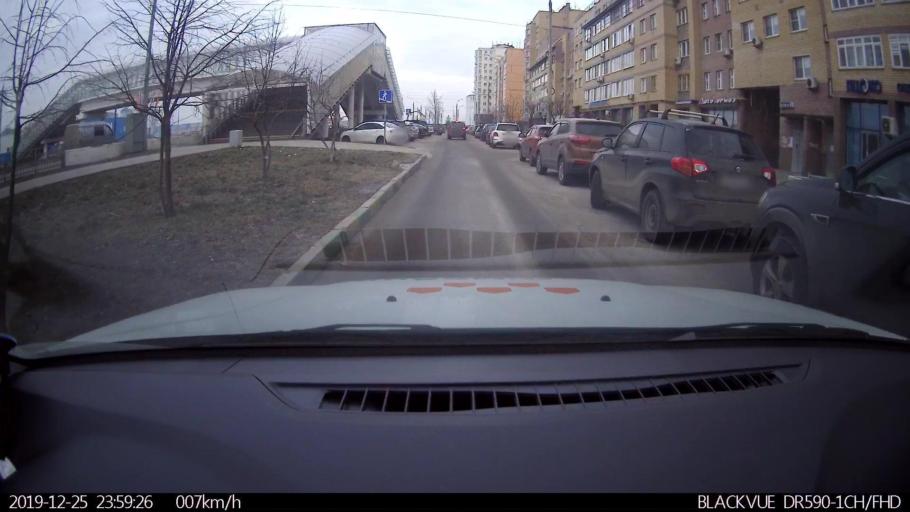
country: RU
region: Nizjnij Novgorod
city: Nizhniy Novgorod
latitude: 56.3338
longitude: 43.9560
